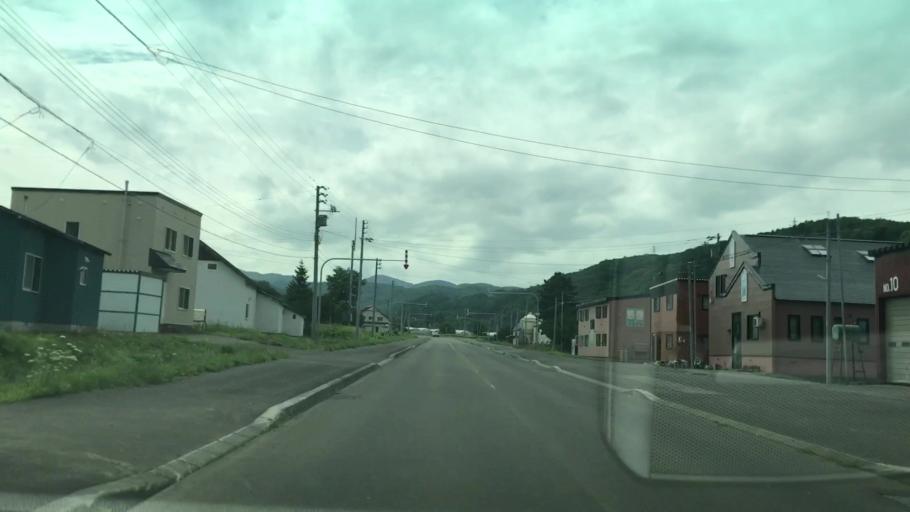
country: JP
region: Hokkaido
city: Yoichi
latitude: 43.1801
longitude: 140.8453
